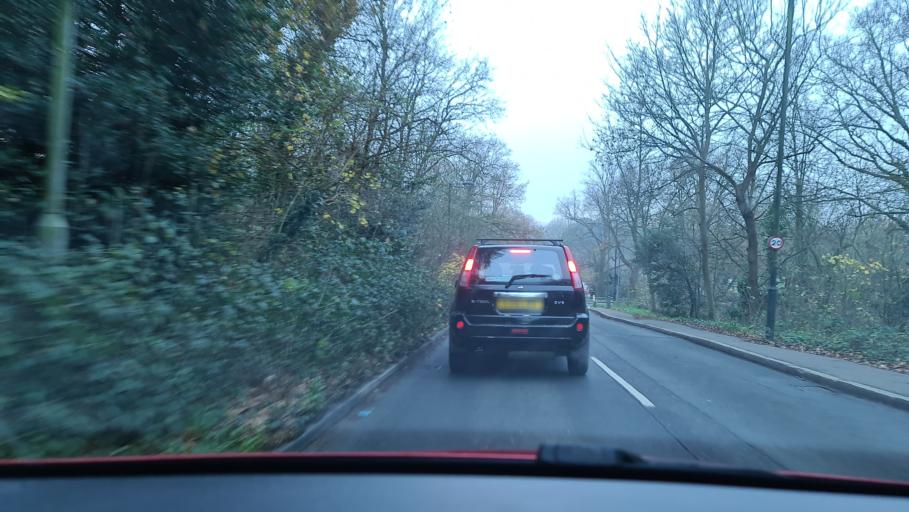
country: GB
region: England
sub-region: Greater London
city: Richmond
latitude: 51.4476
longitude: -0.2978
